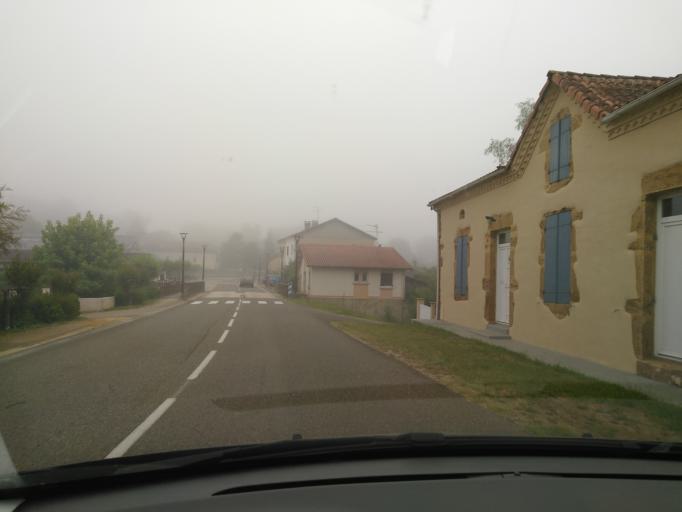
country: FR
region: Aquitaine
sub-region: Departement des Landes
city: Villeneuve-de-Marsan
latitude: 43.8893
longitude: -0.3901
